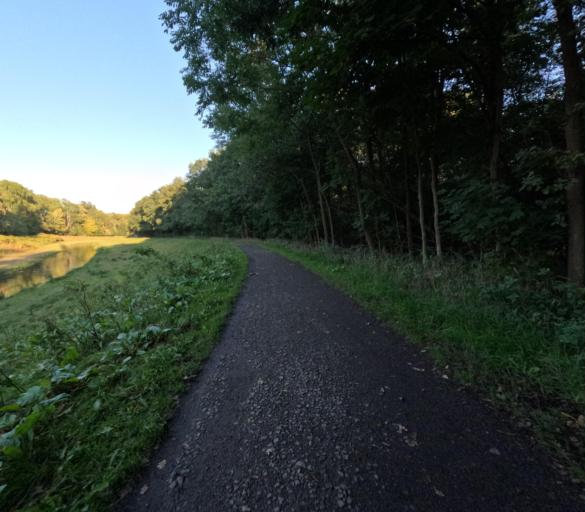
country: DE
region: Saxony
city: Leipzig
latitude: 51.3641
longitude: 12.3188
